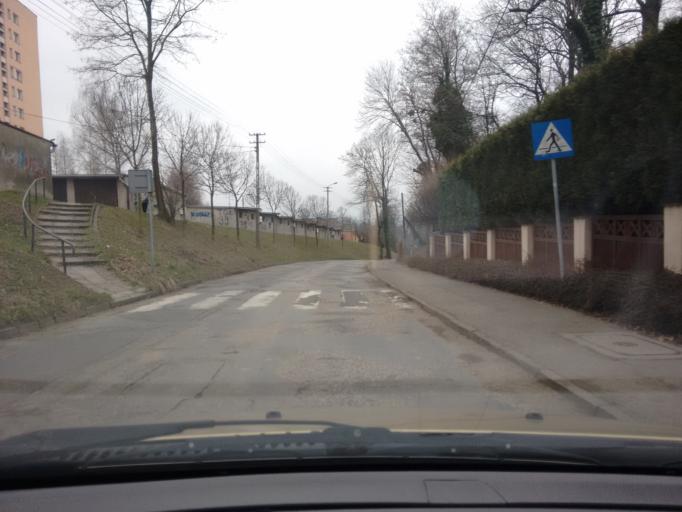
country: PL
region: Silesian Voivodeship
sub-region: Powiat cieszynski
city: Cieszyn
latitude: 49.7570
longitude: 18.6295
